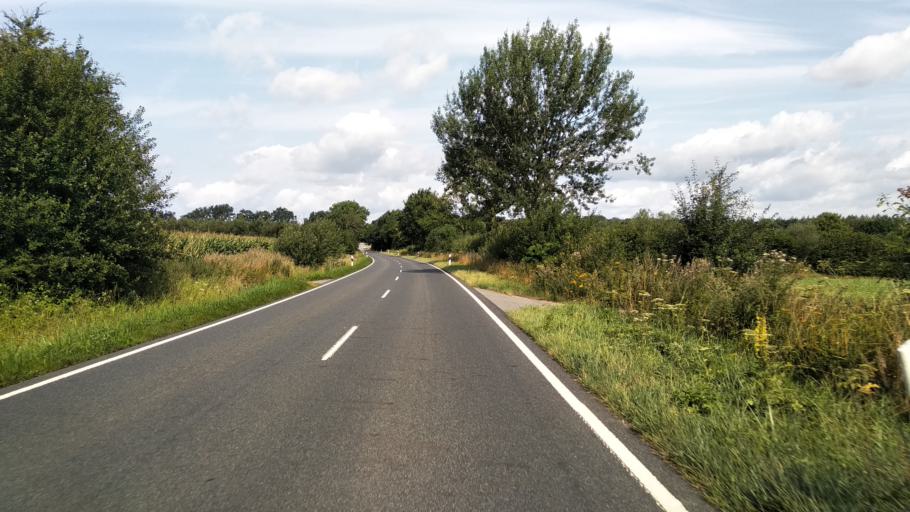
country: DE
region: Schleswig-Holstein
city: Selk
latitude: 54.4638
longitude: 9.5793
